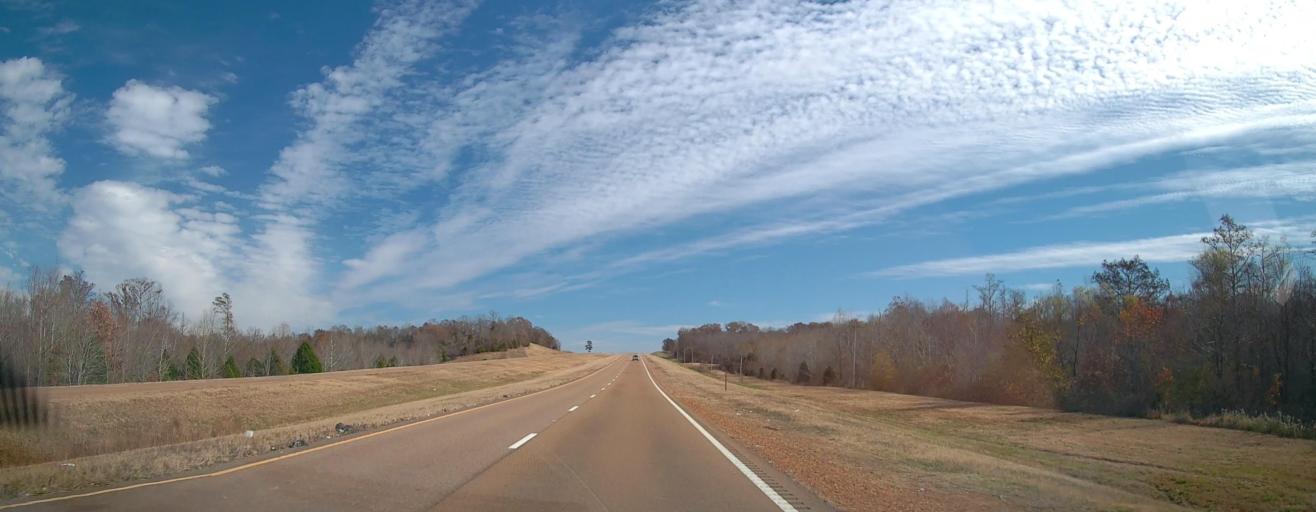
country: US
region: Mississippi
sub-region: Benton County
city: Ashland
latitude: 34.9459
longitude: -89.1931
